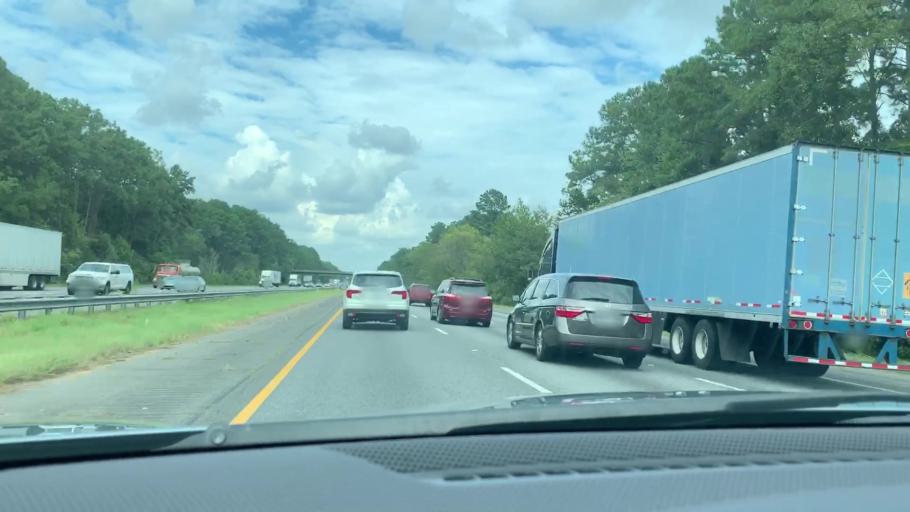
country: US
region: Georgia
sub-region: Chatham County
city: Georgetown
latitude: 32.0247
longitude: -81.2708
